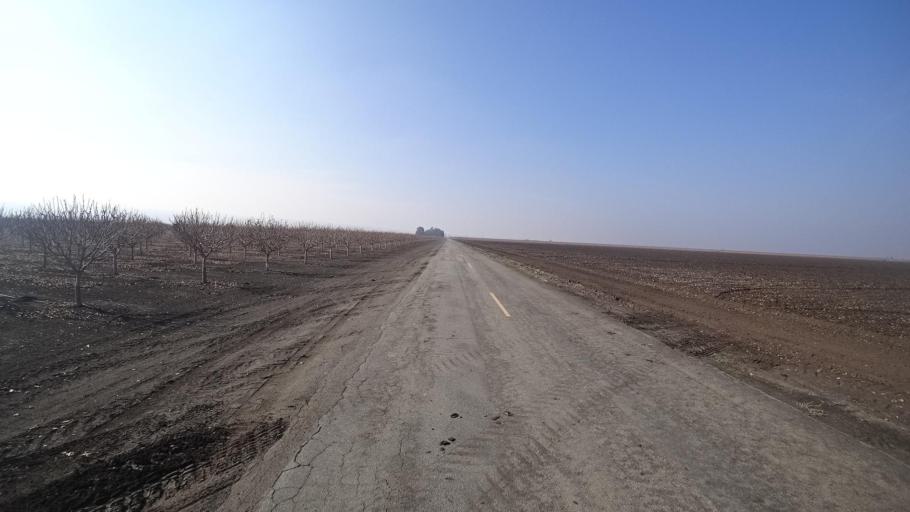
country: US
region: California
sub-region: Kern County
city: Buttonwillow
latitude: 35.3402
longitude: -119.4168
